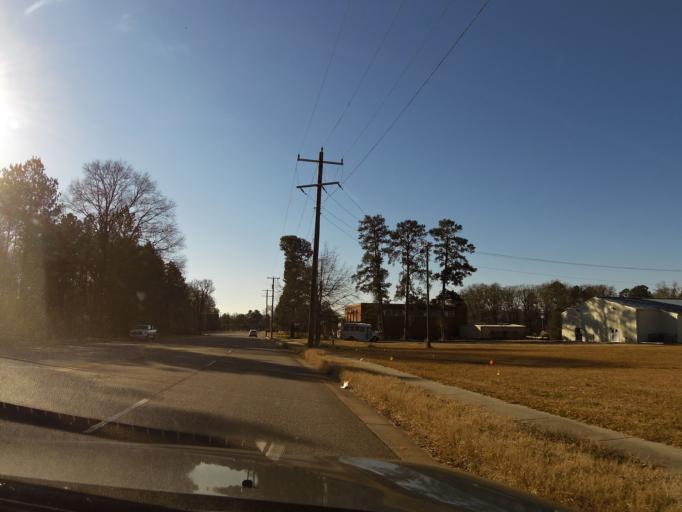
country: US
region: Virginia
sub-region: City of Hopewell
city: Hopewell
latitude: 37.2968
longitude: -77.2904
